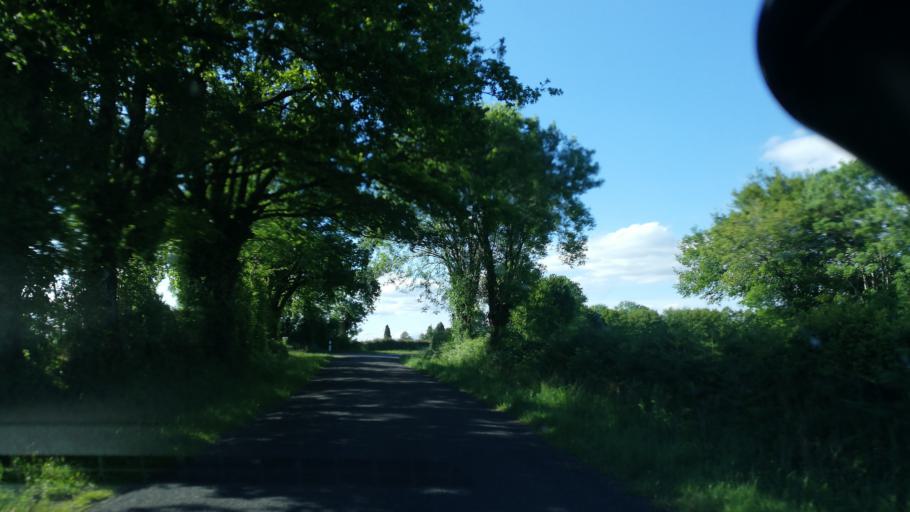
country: FR
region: Poitou-Charentes
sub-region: Departement des Deux-Sevres
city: Moncoutant
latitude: 46.6785
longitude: -0.5721
